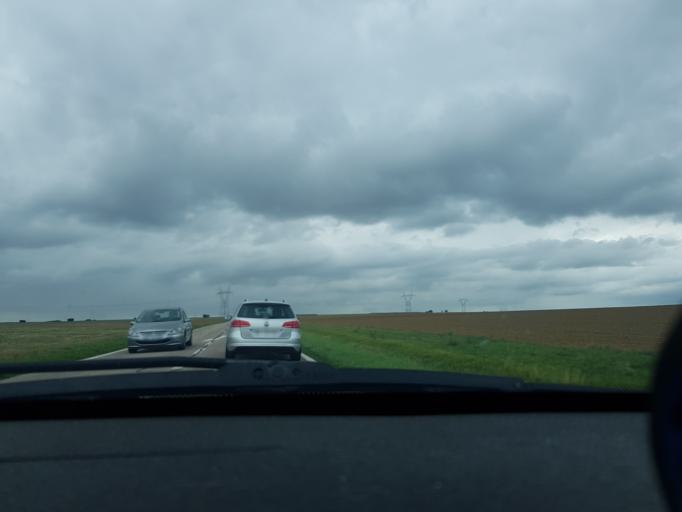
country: FR
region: Lorraine
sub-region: Departement de la Moselle
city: Faulquemont
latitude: 48.9876
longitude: 6.6016
